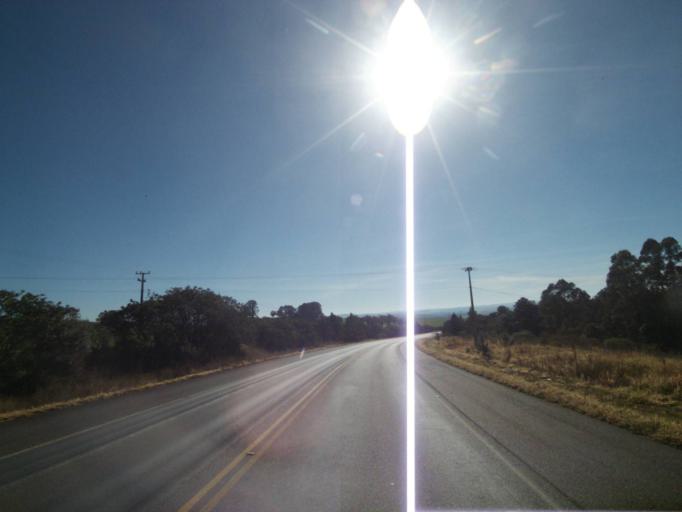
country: BR
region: Parana
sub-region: Tibagi
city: Tibagi
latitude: -24.4950
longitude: -50.4445
